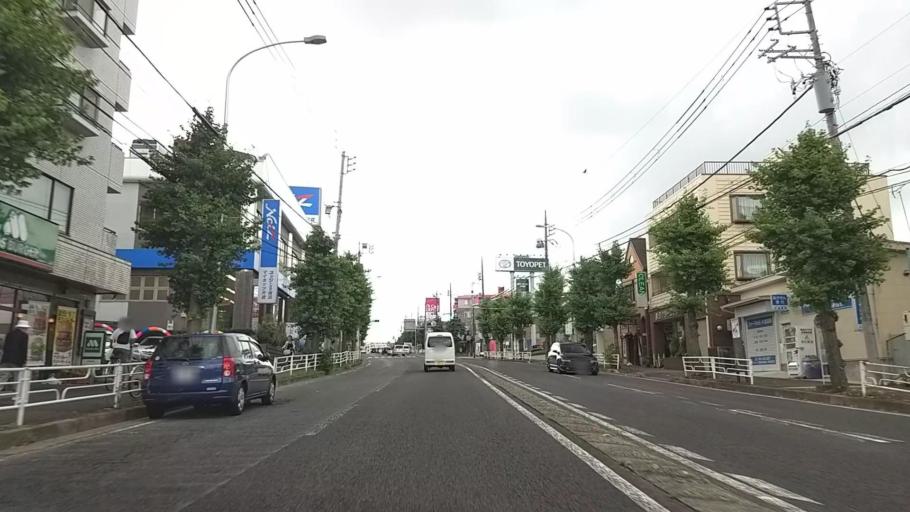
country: JP
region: Kanagawa
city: Yokohama
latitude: 35.4890
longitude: 139.6056
